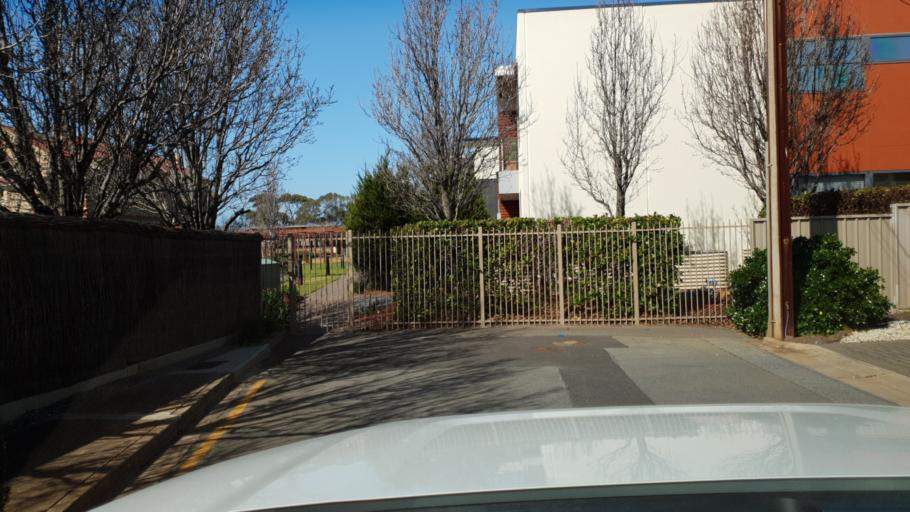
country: AU
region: South Australia
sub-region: Adelaide
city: Brighton
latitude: -35.0120
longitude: 138.5156
